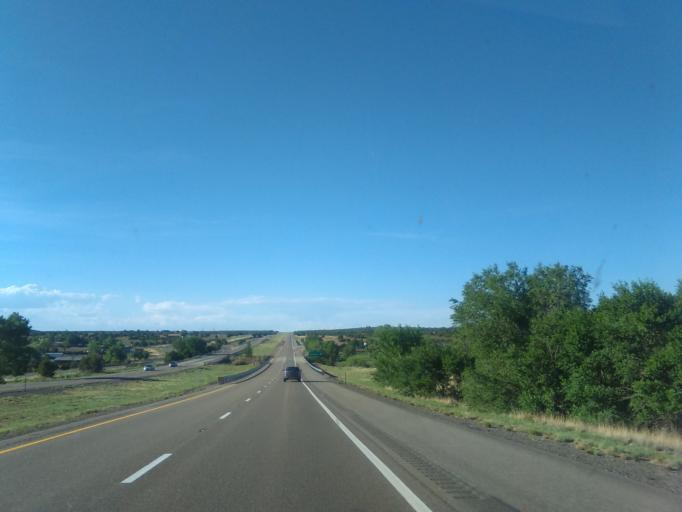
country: US
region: New Mexico
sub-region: San Miguel County
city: Las Vegas
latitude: 35.4553
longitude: -105.2779
